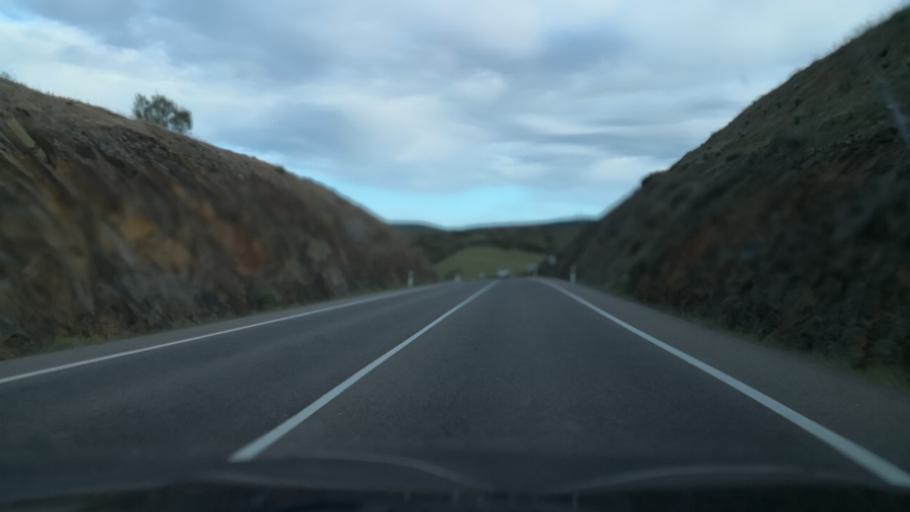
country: ES
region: Extremadura
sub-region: Provincia de Caceres
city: Pedroso de Acim
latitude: 39.8358
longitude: -6.3921
